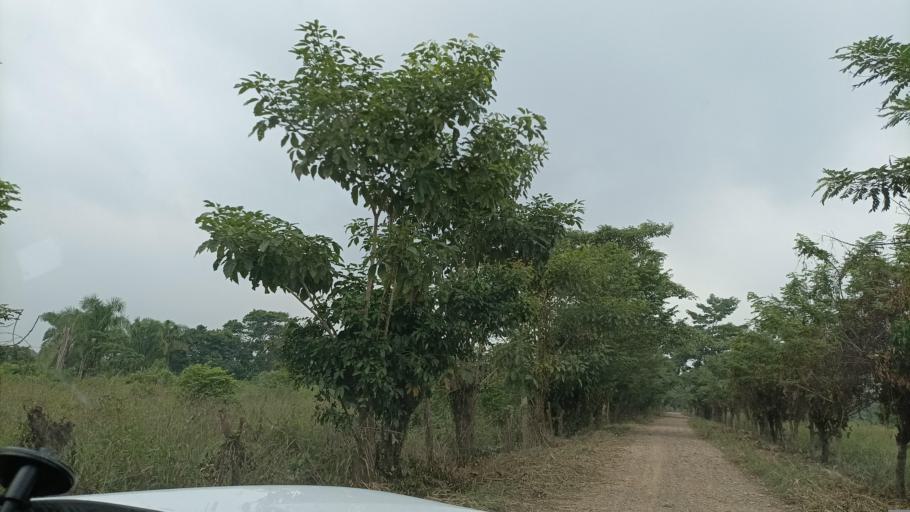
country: MX
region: Veracruz
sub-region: Uxpanapa
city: Poblado 10
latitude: 17.5664
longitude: -94.2259
